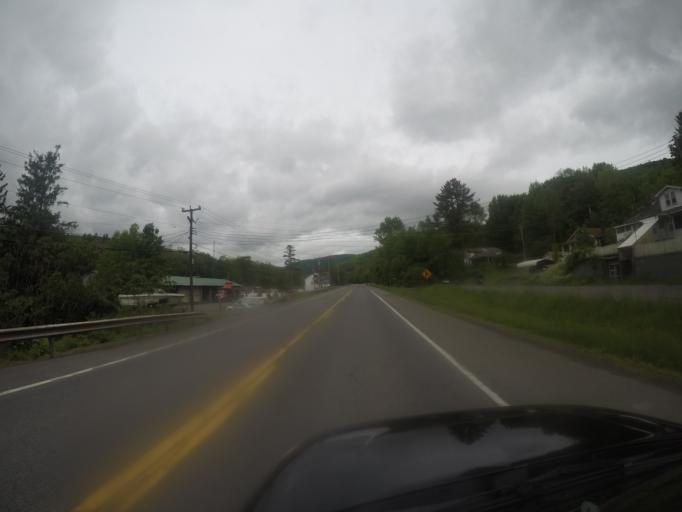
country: US
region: New York
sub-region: Ulster County
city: Shokan
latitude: 42.1158
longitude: -74.3684
